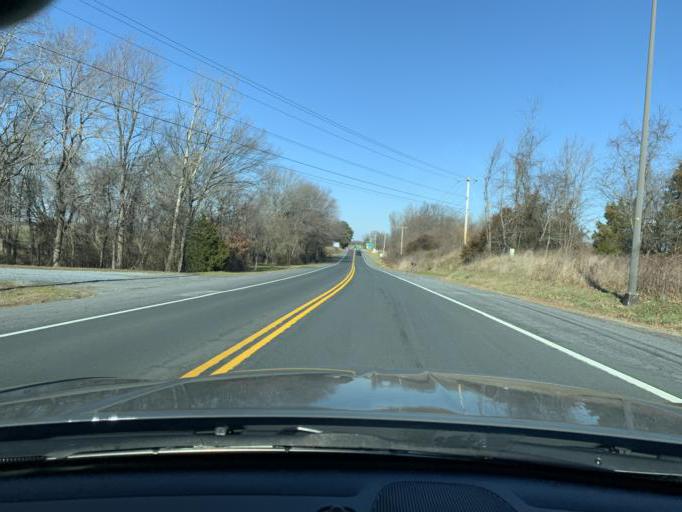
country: US
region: Maryland
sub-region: Queen Anne's County
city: Centreville
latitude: 39.0185
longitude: -76.0765
